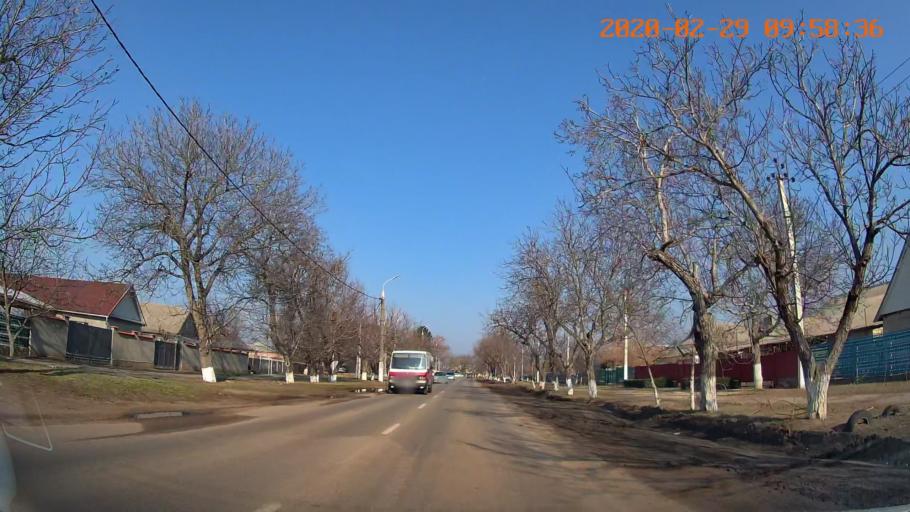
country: MD
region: Telenesti
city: Slobozia
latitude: 46.7502
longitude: 29.6907
